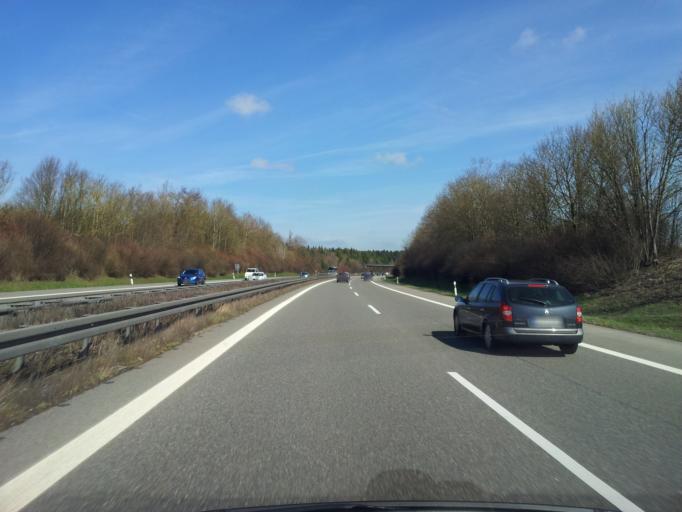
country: DE
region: Baden-Wuerttemberg
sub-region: Karlsruhe Region
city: Empfingen
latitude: 48.4078
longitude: 8.7263
